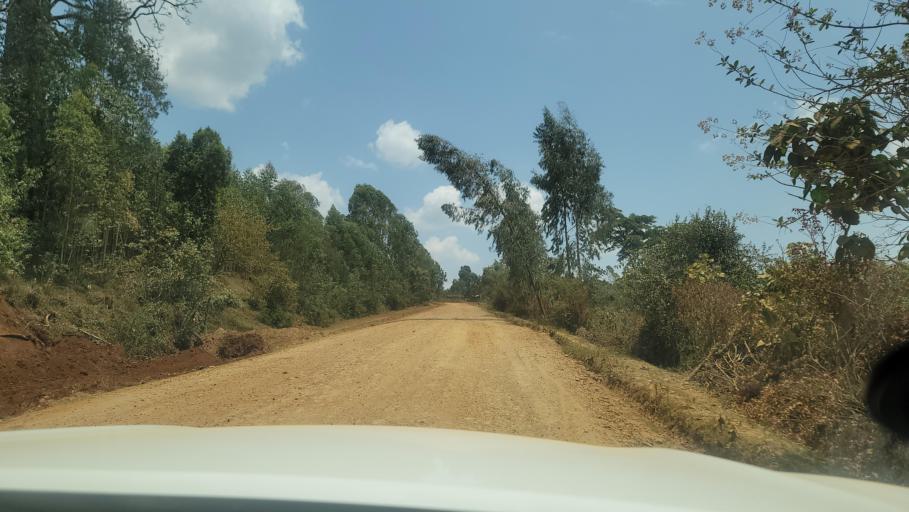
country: ET
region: Oromiya
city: Agaro
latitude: 7.7998
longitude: 36.4567
